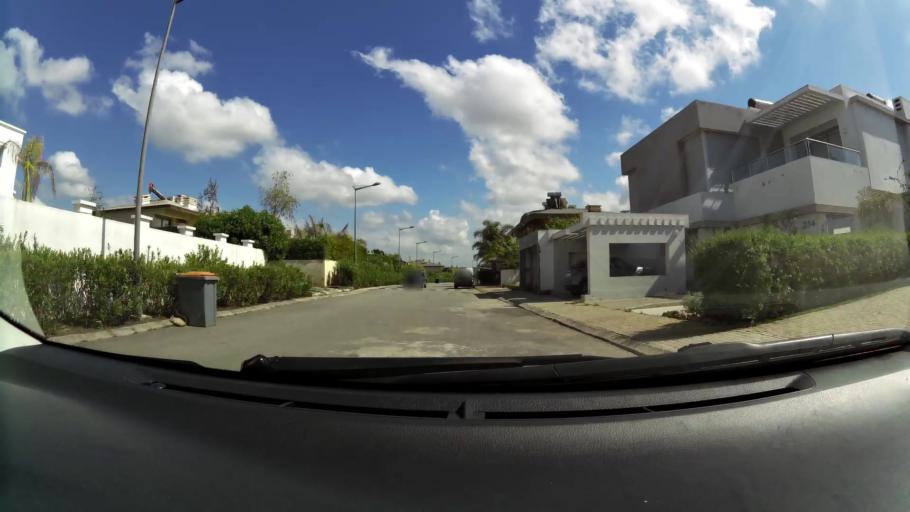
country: MA
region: Grand Casablanca
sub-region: Nouaceur
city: Bouskoura
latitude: 33.4681
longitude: -7.5962
